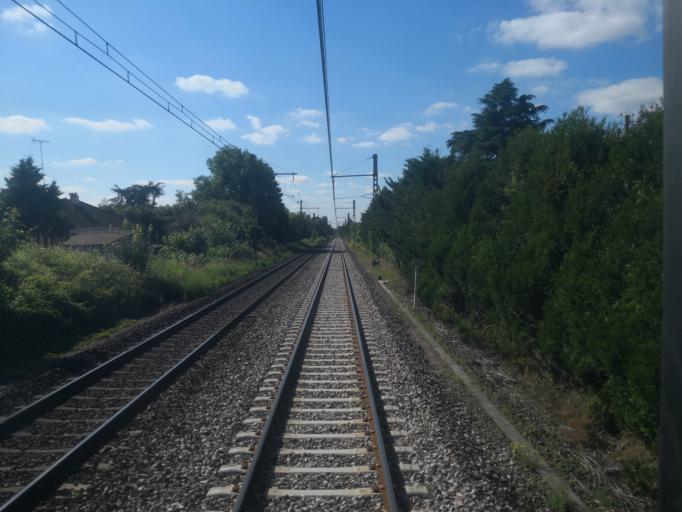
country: FR
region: Ile-de-France
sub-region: Departement de Seine-et-Marne
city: Bois-le-Roi
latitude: 48.4690
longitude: 2.7023
